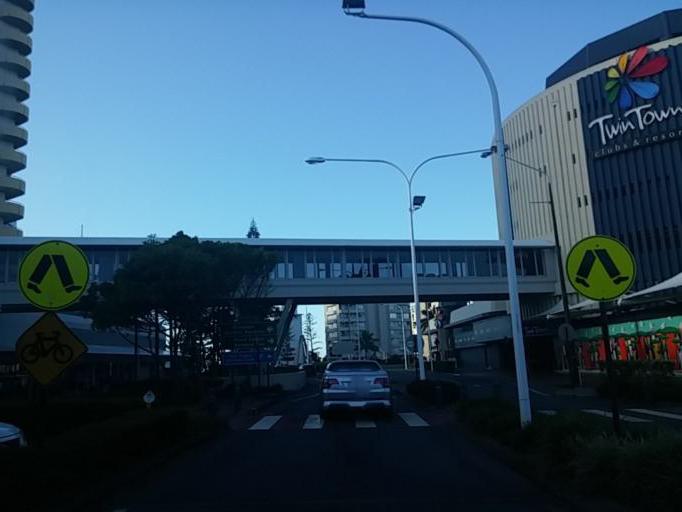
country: AU
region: New South Wales
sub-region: Tweed
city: Tweed Heads West
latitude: -28.1693
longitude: 153.5437
